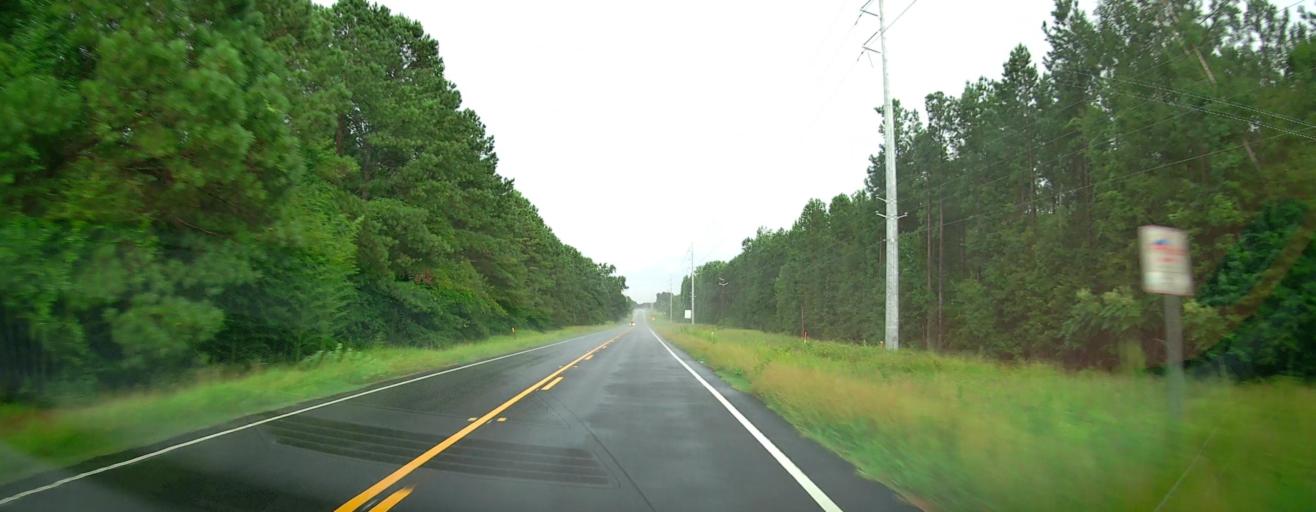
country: US
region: Georgia
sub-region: Twiggs County
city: Jeffersonville
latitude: 32.5810
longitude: -83.2139
